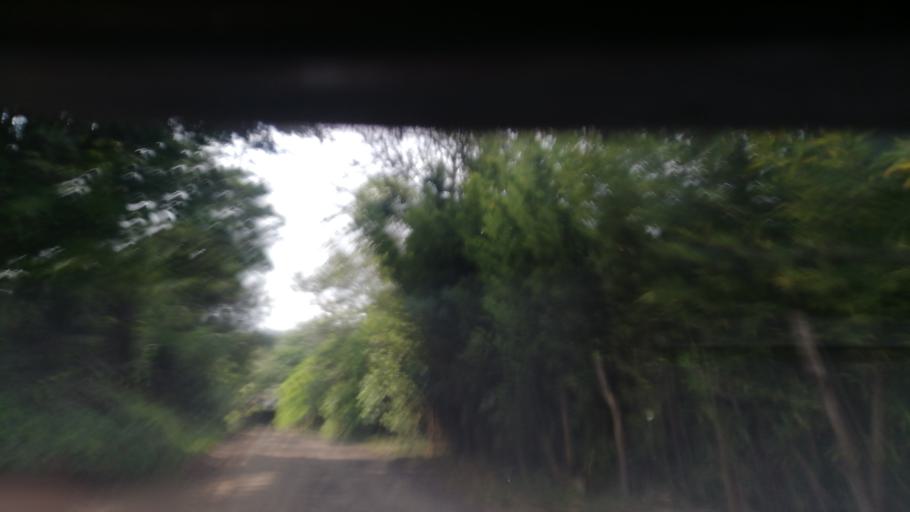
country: CO
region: Valle del Cauca
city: Cali
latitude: 3.4963
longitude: -76.5459
